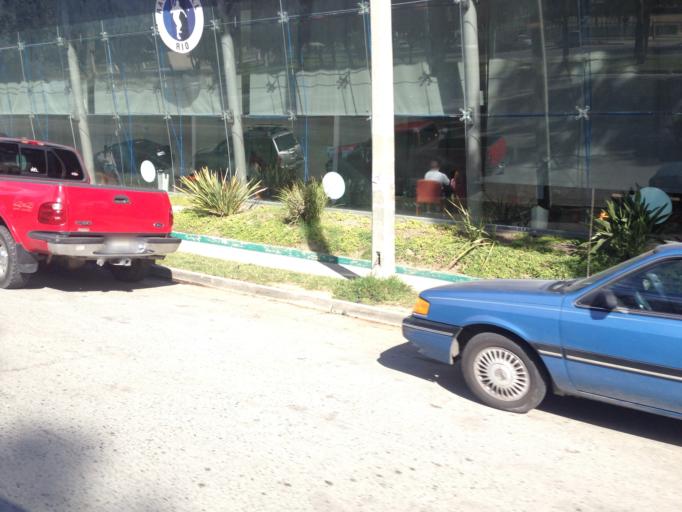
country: MX
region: Baja California
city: Tijuana
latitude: 32.5287
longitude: -117.0116
